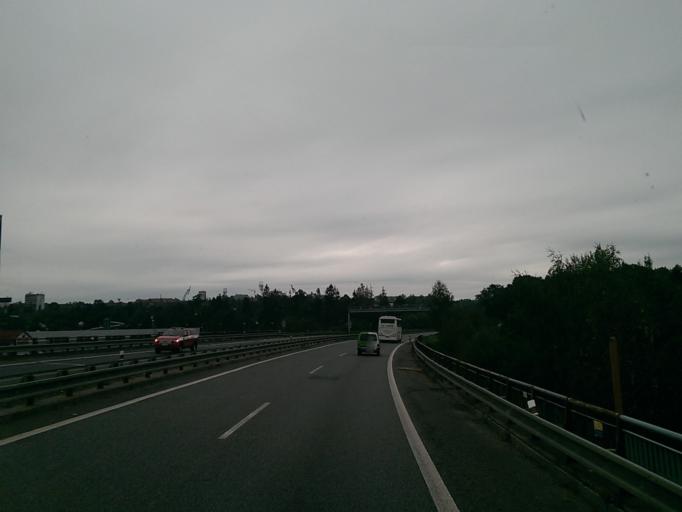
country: CZ
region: Vysocina
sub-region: Okres Jihlava
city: Jihlava
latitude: 49.4113
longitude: 15.5781
